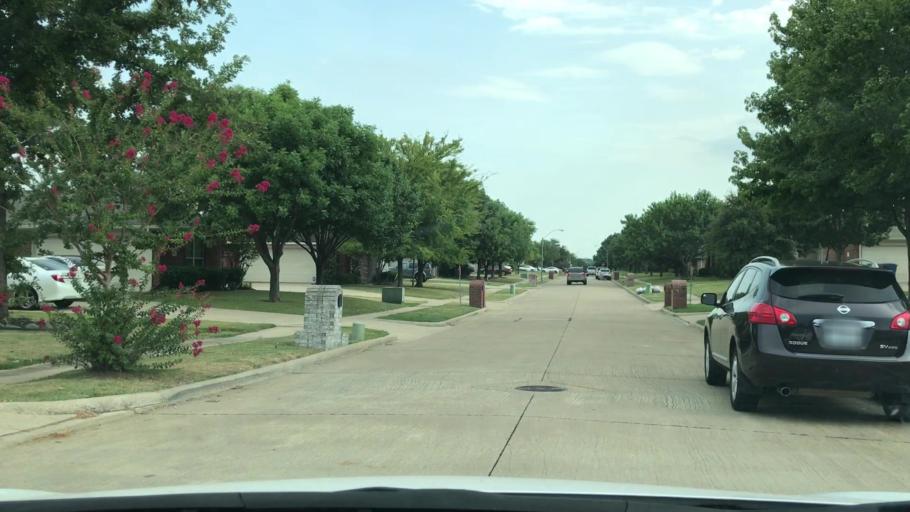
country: US
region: Texas
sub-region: Collin County
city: Wylie
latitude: 33.0166
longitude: -96.5174
